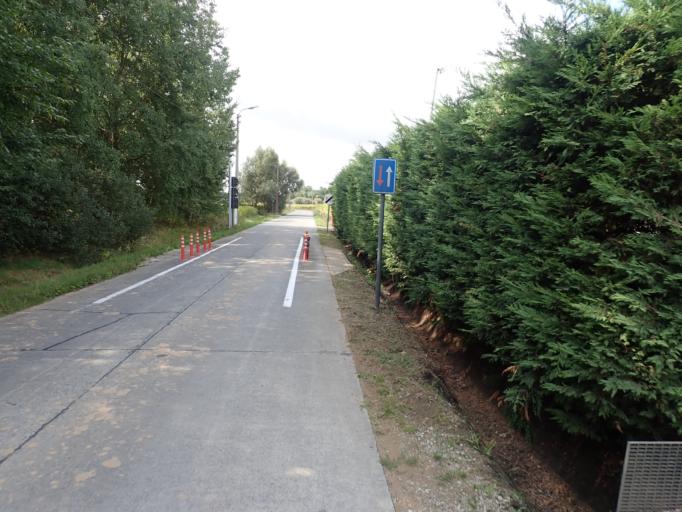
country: BE
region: Flanders
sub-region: Provincie Vlaams-Brabant
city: Londerzeel
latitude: 51.0310
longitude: 4.3171
